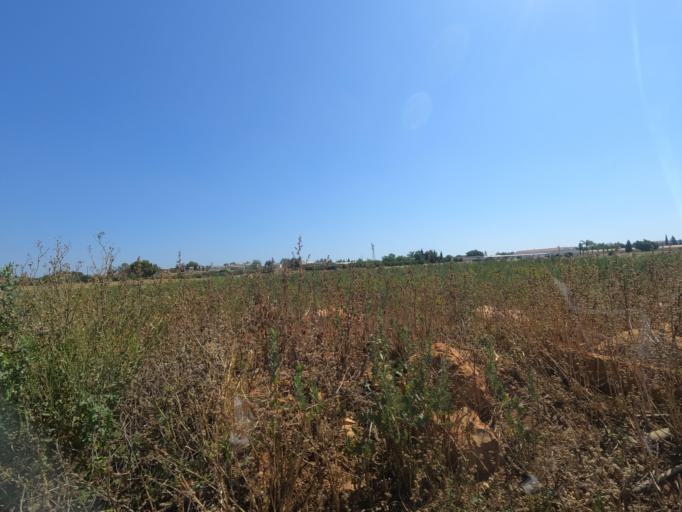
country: CY
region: Ammochostos
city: Frenaros
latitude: 35.0223
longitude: 33.9226
